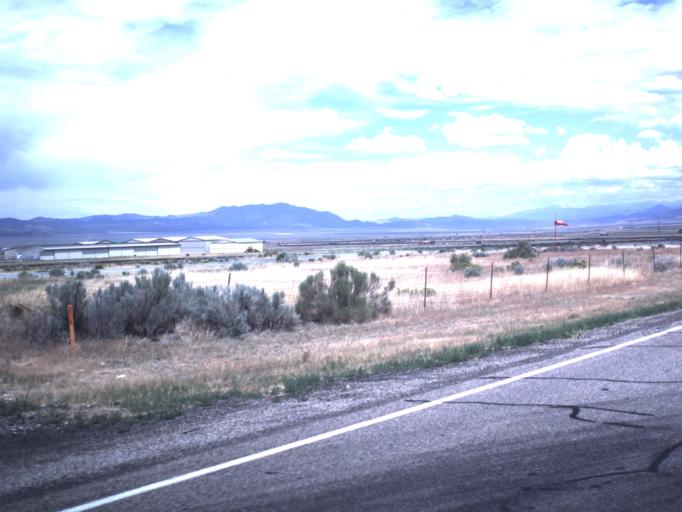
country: US
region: Utah
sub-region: Iron County
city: Parowan
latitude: 37.8551
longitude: -112.8206
